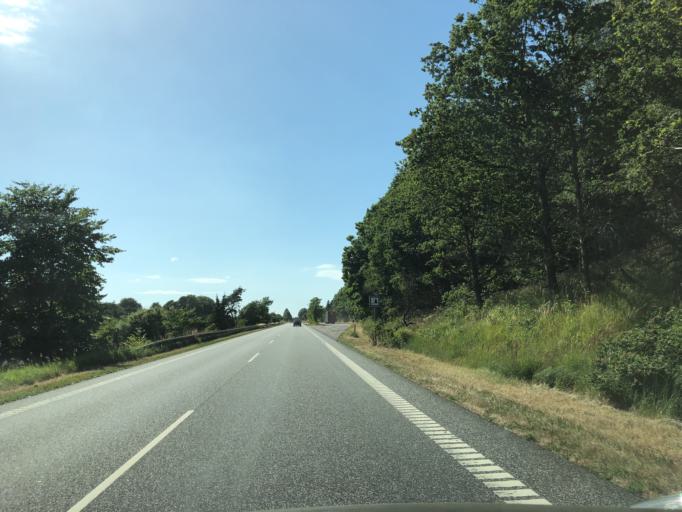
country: DK
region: North Denmark
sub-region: Vesthimmerland Kommune
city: Alestrup
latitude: 56.6117
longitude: 9.4033
